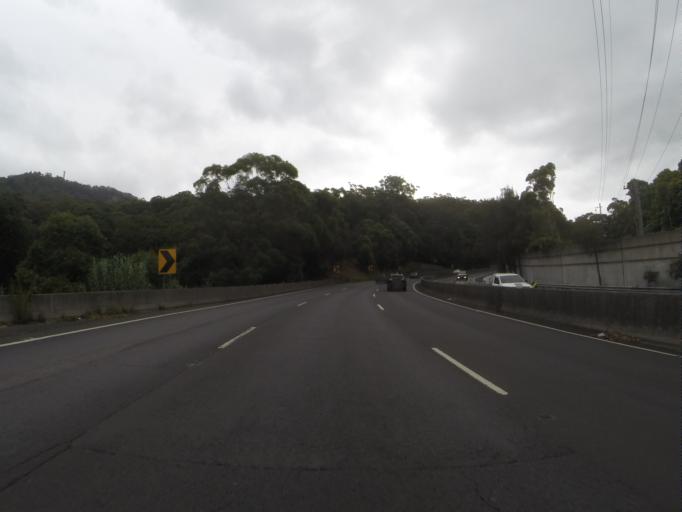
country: AU
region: New South Wales
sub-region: Wollongong
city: Mount Ousley
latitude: -34.4010
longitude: 150.8696
